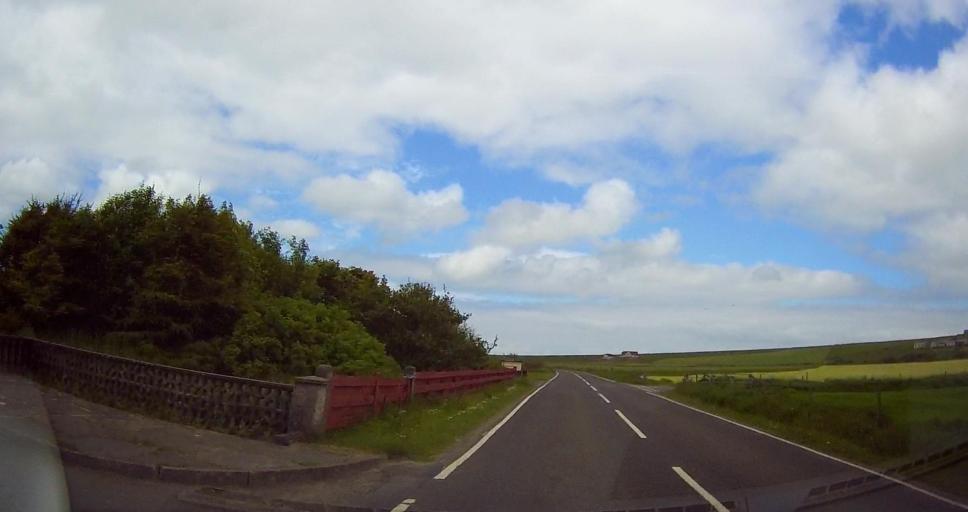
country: GB
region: Scotland
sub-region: Orkney Islands
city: Stromness
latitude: 59.0860
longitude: -3.2559
